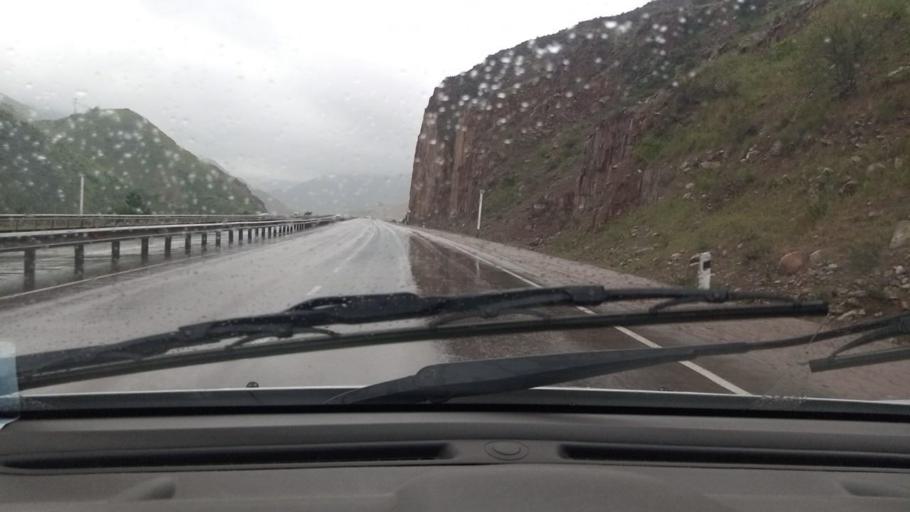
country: UZ
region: Toshkent
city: Angren
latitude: 41.1210
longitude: 70.3496
